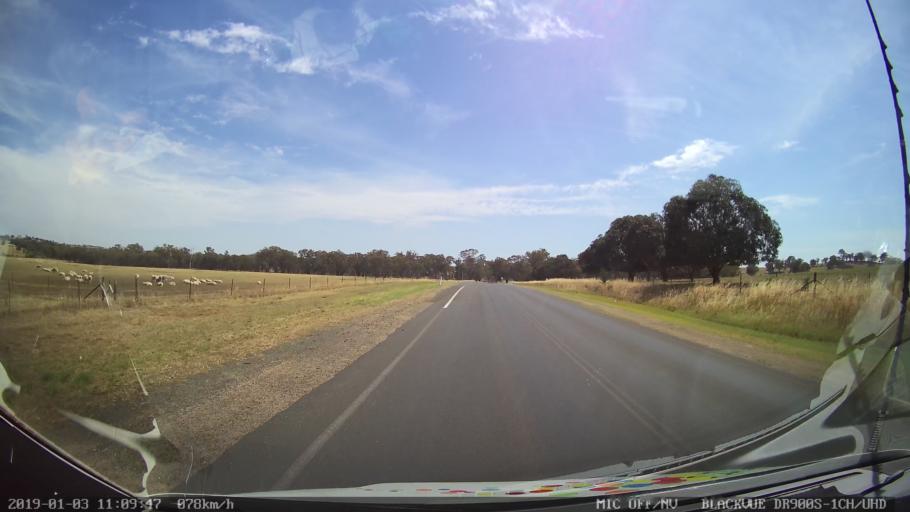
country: AU
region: New South Wales
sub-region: Young
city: Young
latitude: -34.2341
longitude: 148.2560
